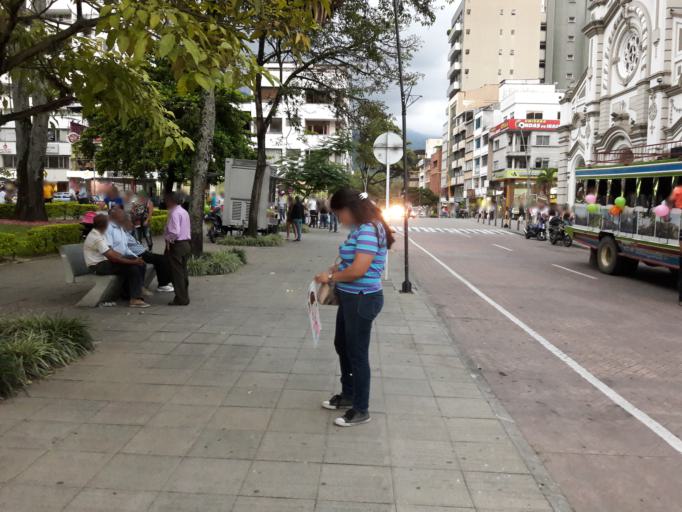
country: CO
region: Tolima
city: Ibague
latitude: 4.4444
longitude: -75.2428
